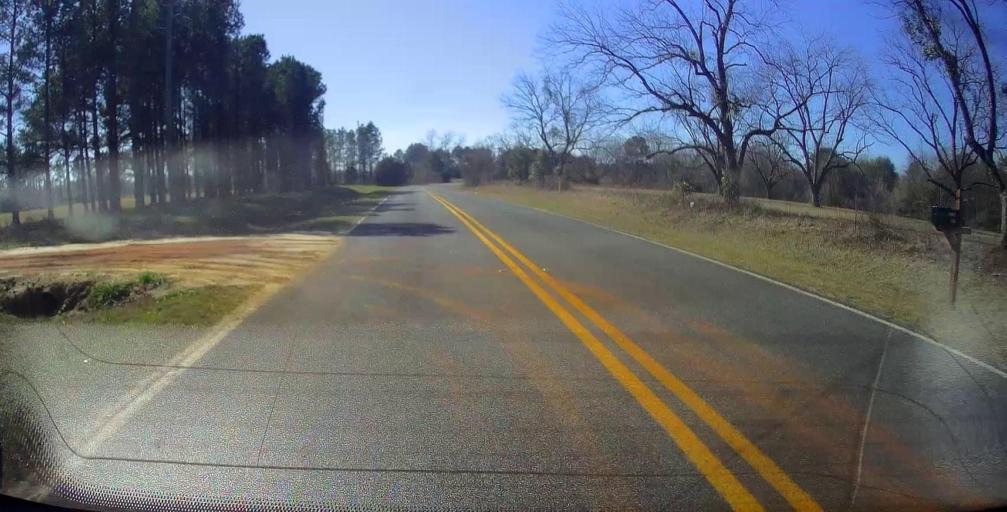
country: US
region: Georgia
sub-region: Macon County
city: Montezuma
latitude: 32.2784
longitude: -84.0082
